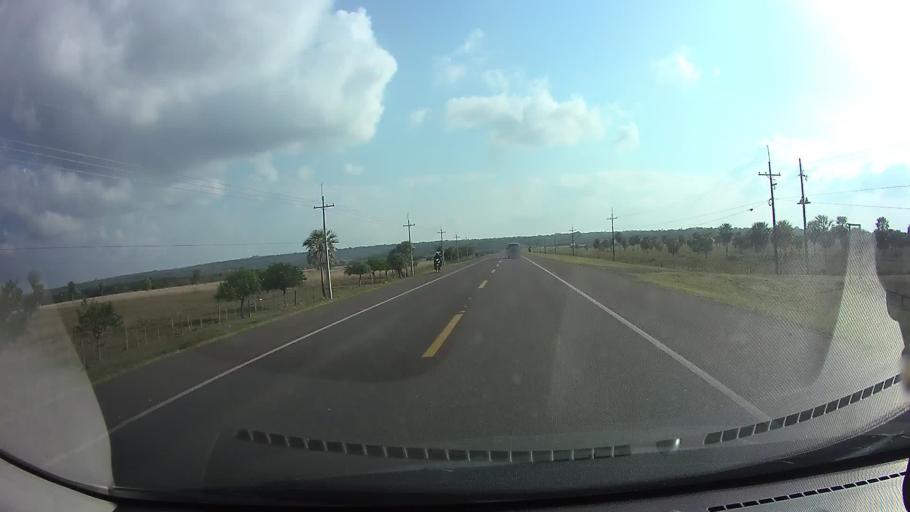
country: PY
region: Cordillera
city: Emboscada
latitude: -25.0848
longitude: -57.2847
